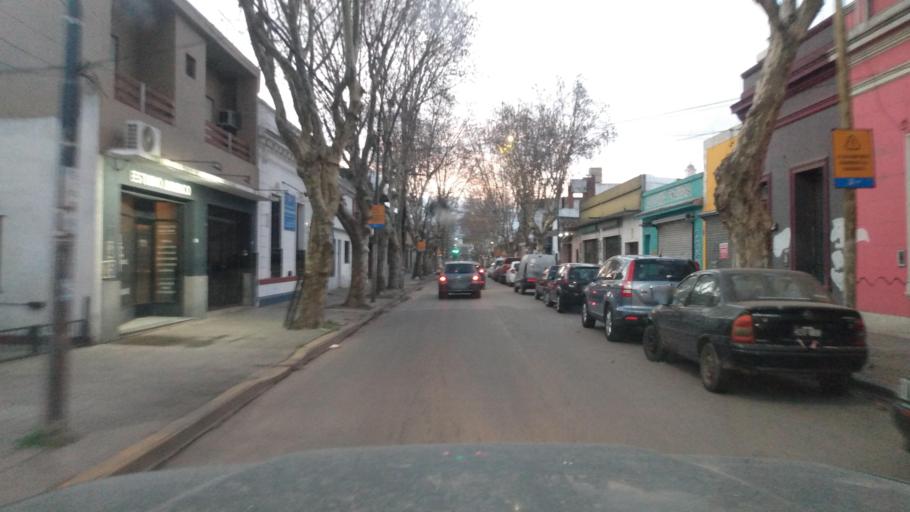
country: AR
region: Buenos Aires
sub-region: Partido de Pilar
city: Pilar
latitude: -34.4615
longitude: -58.9145
